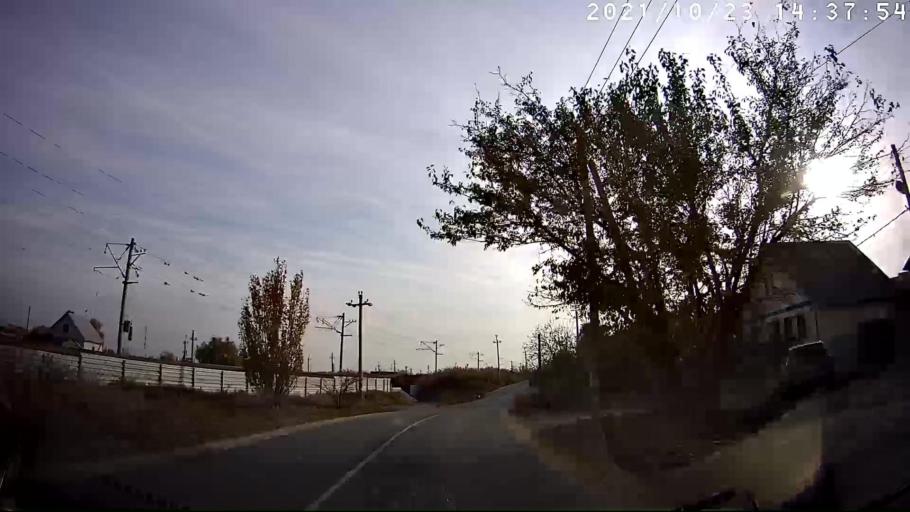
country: RU
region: Volgograd
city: Krasnoslobodsk
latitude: 48.4950
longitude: 44.5498
